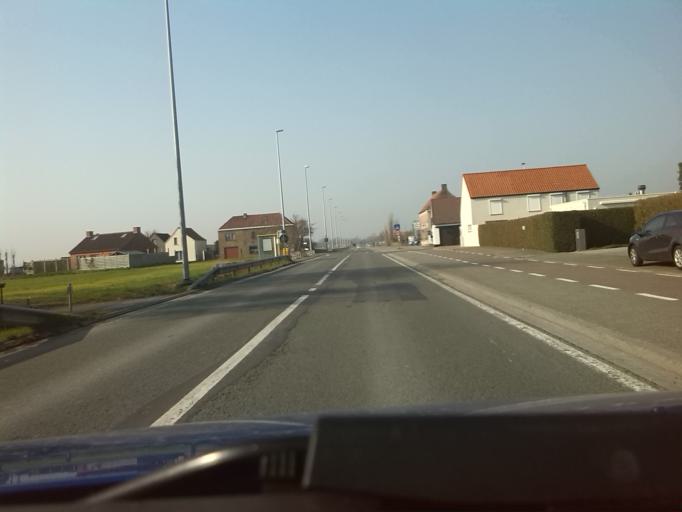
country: BE
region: Flanders
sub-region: Provincie West-Vlaanderen
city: Wenduine
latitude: 51.2671
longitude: 3.0962
